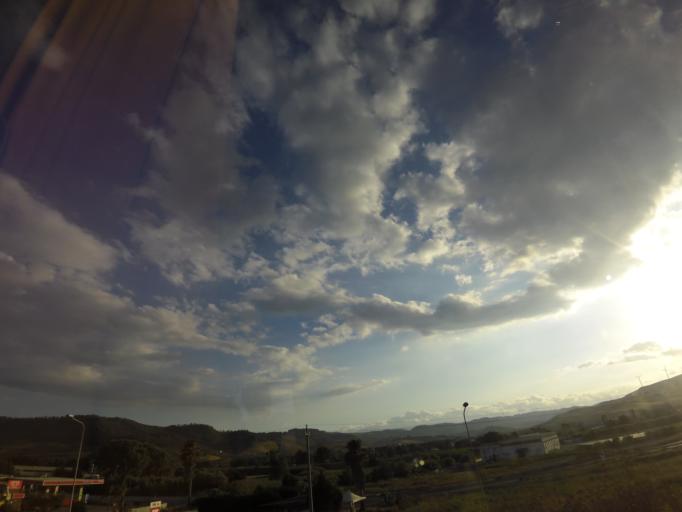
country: IT
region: Calabria
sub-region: Provincia di Catanzaro
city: Catanzaro
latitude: 38.8627
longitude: 16.5679
